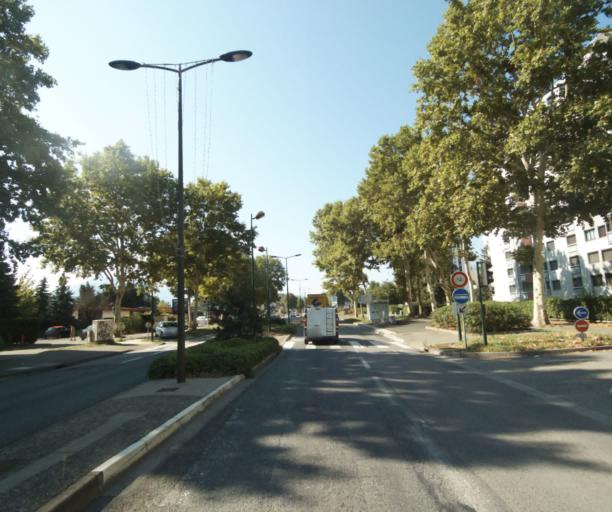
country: FR
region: Rhone-Alpes
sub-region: Departement de l'Isere
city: Le Pont-de-Claix
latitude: 45.1358
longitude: 5.7014
